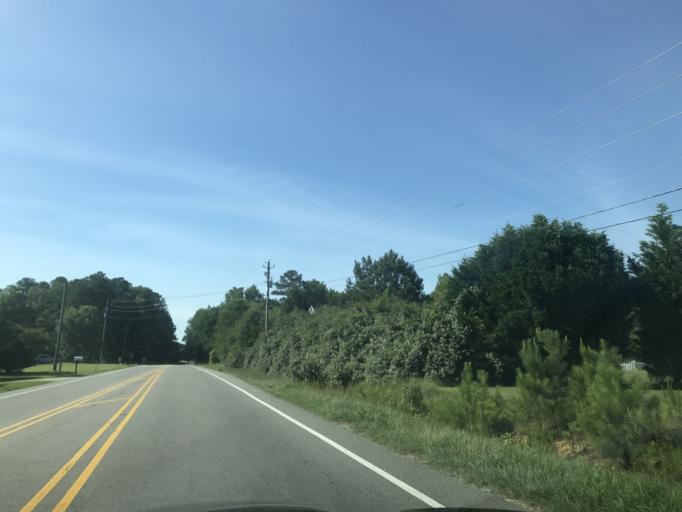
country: US
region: North Carolina
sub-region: Johnston County
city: Clayton
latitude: 35.6188
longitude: -78.5357
